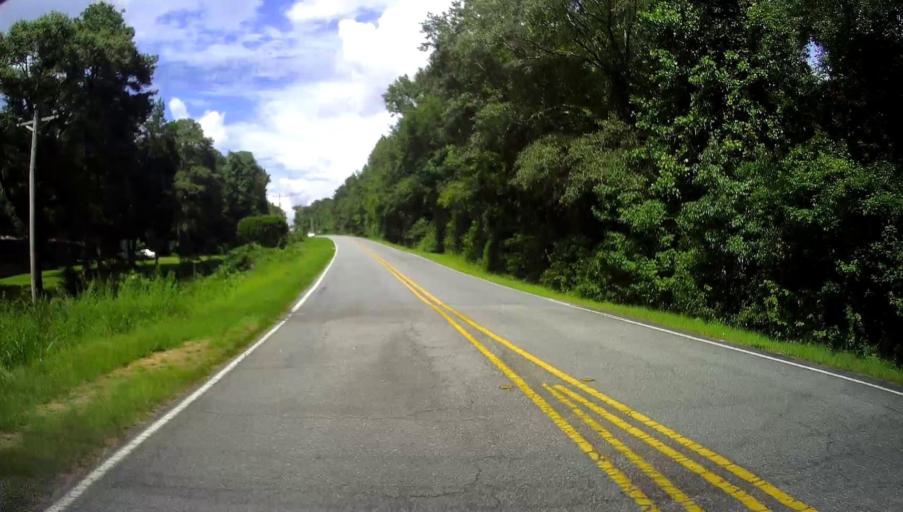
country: US
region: Georgia
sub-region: Chattahoochee County
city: Cusseta
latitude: 32.3016
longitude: -84.7793
